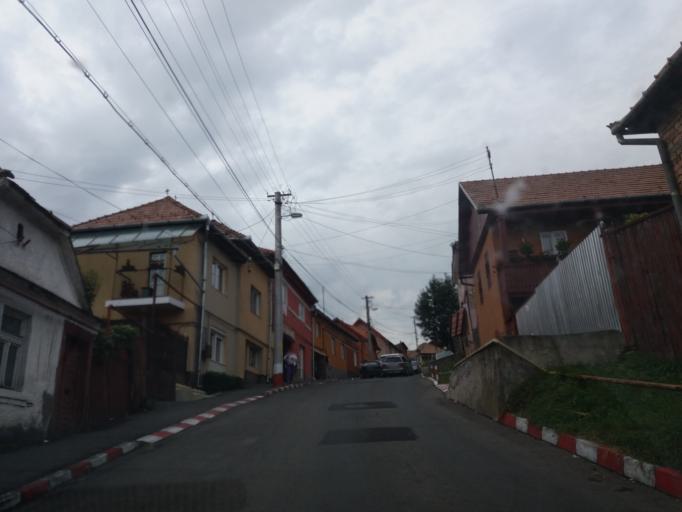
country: RO
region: Mures
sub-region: Municipiul Reghin
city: Reghin
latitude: 46.7759
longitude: 24.7006
